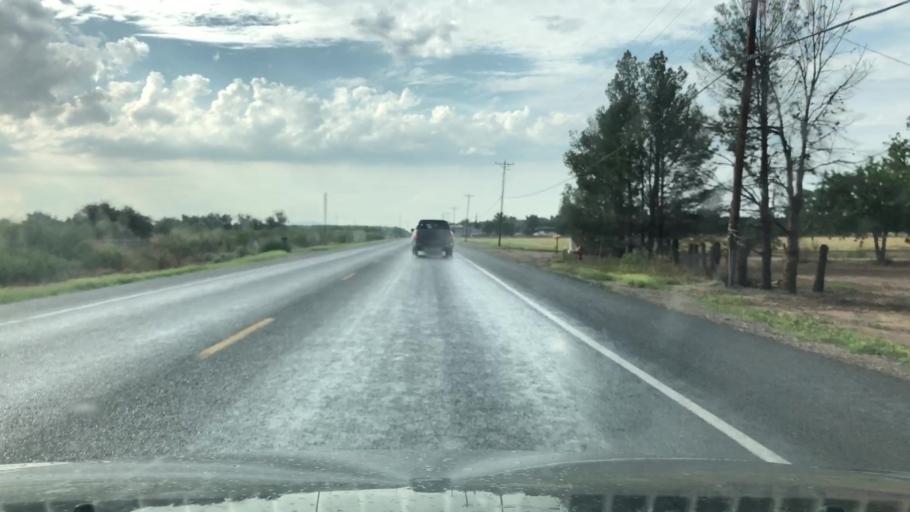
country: US
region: New Mexico
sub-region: Dona Ana County
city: Mesquite
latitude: 32.2057
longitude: -106.7225
